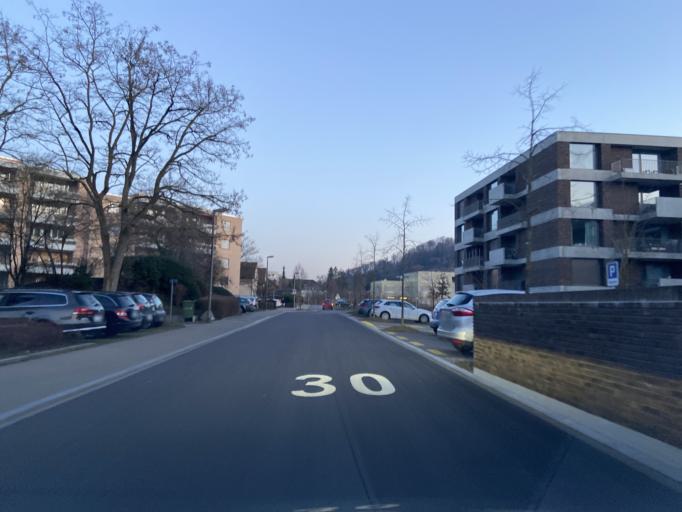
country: CH
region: Zurich
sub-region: Bezirk Winterthur
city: Wuelflingen (Kreis 6) / Niederfeld
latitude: 47.5090
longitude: 8.6808
